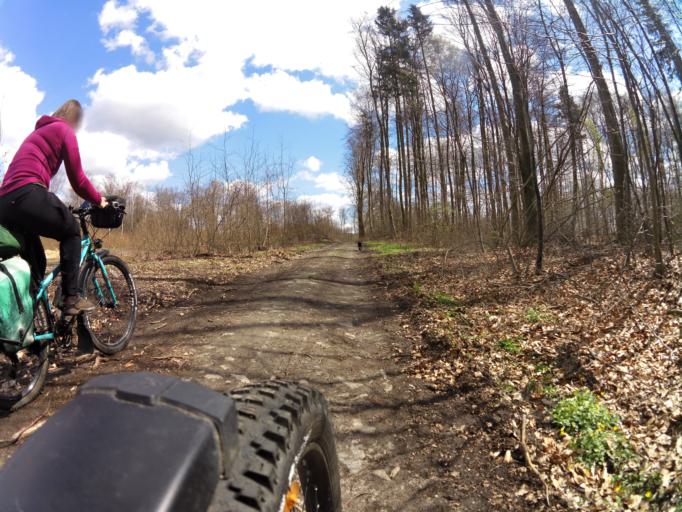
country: PL
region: West Pomeranian Voivodeship
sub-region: Powiat gryficki
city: Gryfice
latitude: 53.8436
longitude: 15.1790
